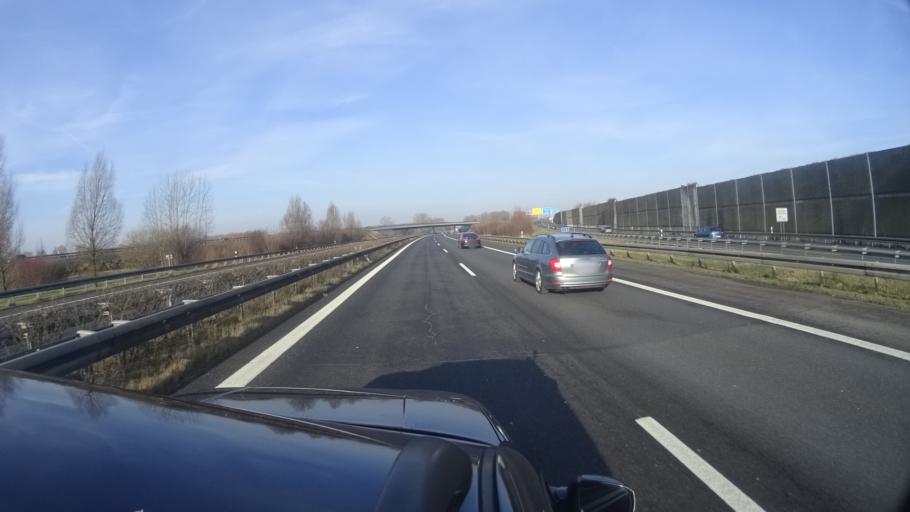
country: DE
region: Brandenburg
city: Velten
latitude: 52.6966
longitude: 13.1999
